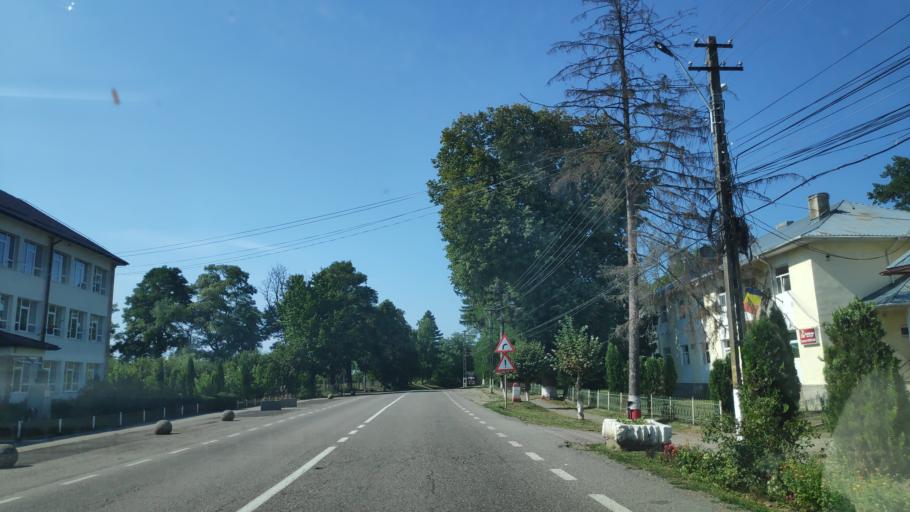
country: RO
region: Suceava
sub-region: Comuna Boroaia
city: Boroaia
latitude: 47.3493
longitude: 26.3361
